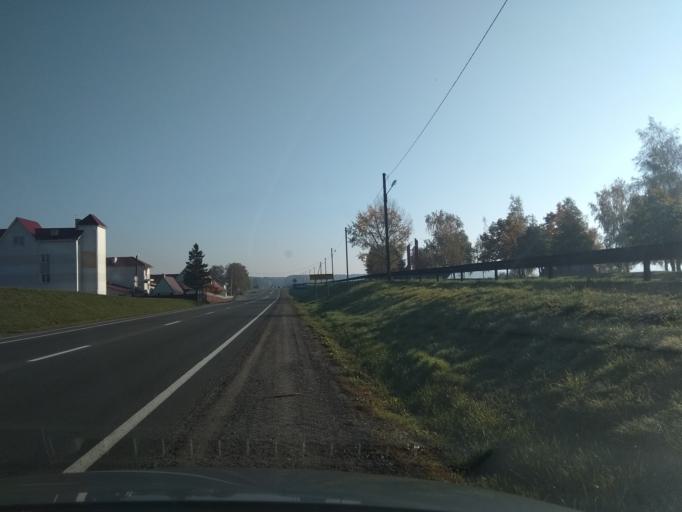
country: BY
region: Grodnenskaya
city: Zel'va
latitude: 53.1436
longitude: 24.8237
